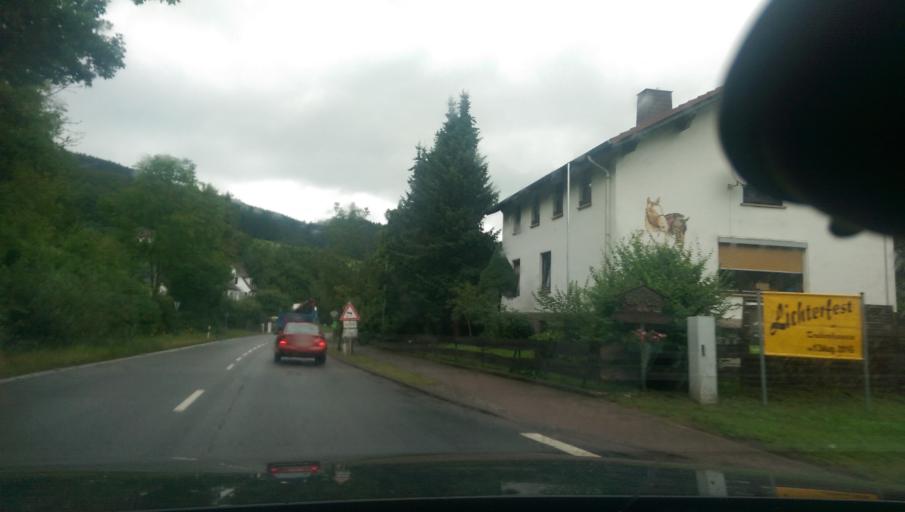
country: DE
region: Hesse
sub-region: Regierungsbezirk Kassel
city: Grossalmerode
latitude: 51.2655
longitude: 9.8330
